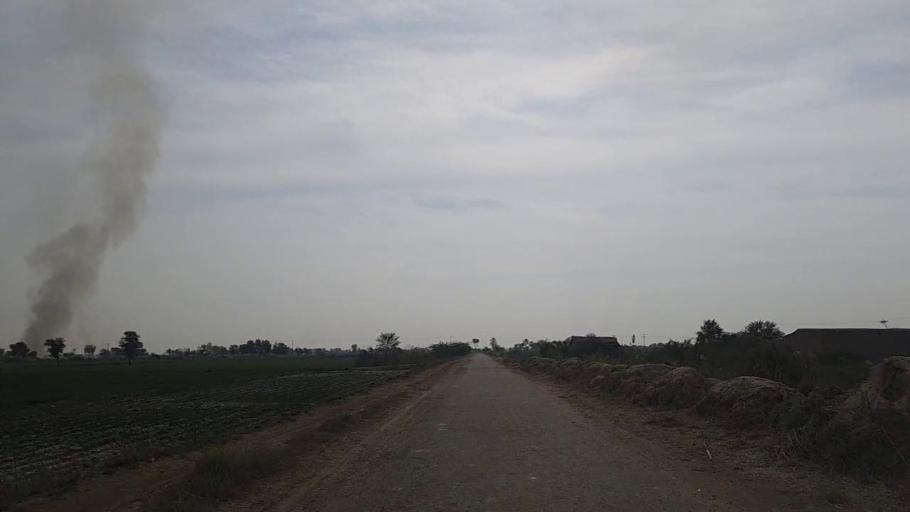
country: PK
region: Sindh
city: Daur
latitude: 26.4546
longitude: 68.4353
